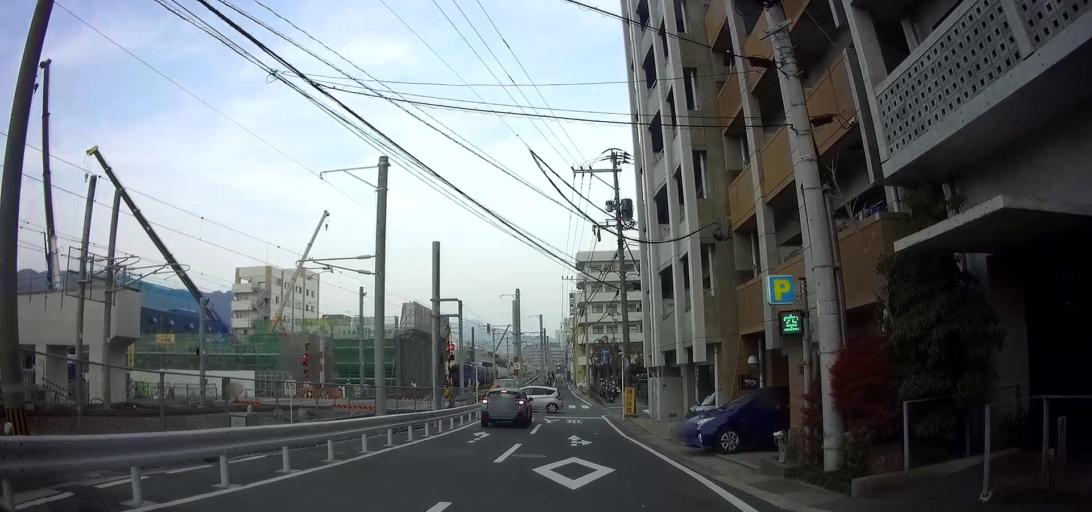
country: JP
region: Nagasaki
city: Nagasaki-shi
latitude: 32.7568
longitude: 129.8683
